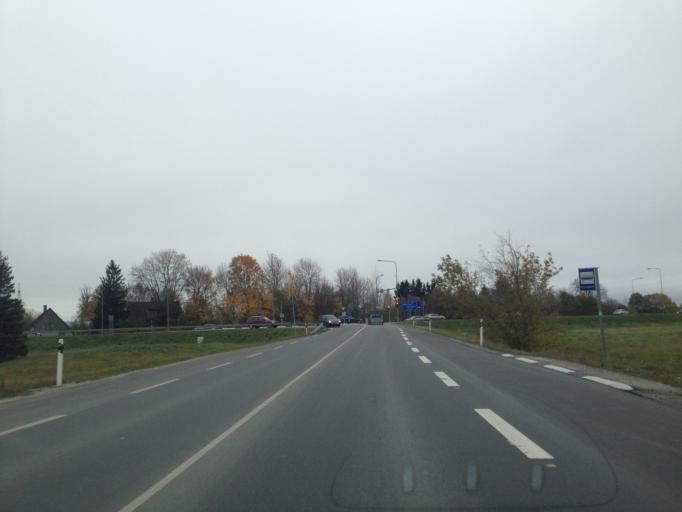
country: EE
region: Harju
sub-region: Harku vald
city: Tabasalu
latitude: 59.3904
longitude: 24.5568
